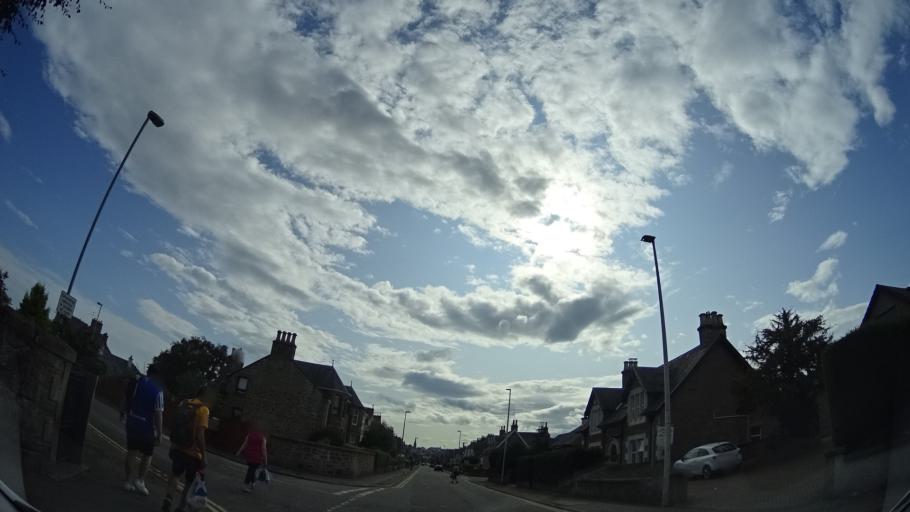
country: GB
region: Scotland
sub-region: Highland
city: Inverness
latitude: 57.4778
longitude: -4.2402
